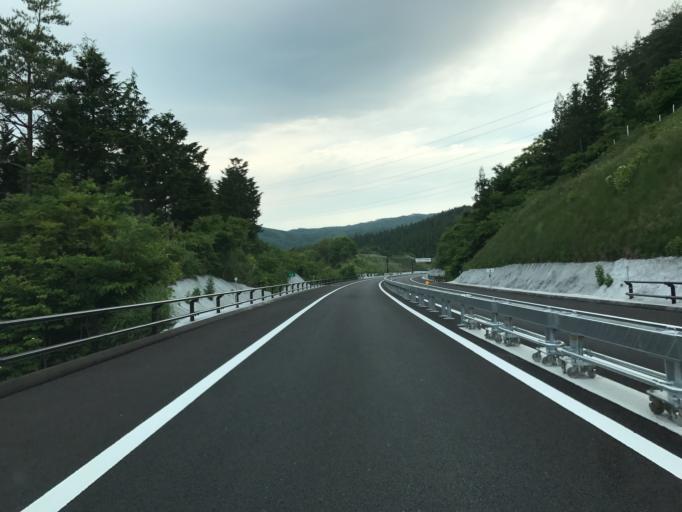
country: JP
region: Miyagi
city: Marumori
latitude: 37.7877
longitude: 140.7599
